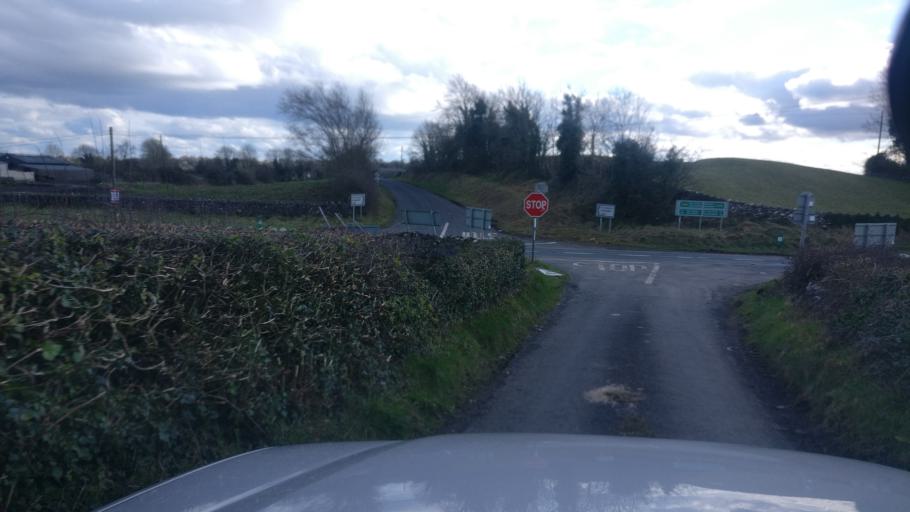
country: IE
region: Connaught
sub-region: County Galway
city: Loughrea
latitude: 53.2000
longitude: -8.4309
